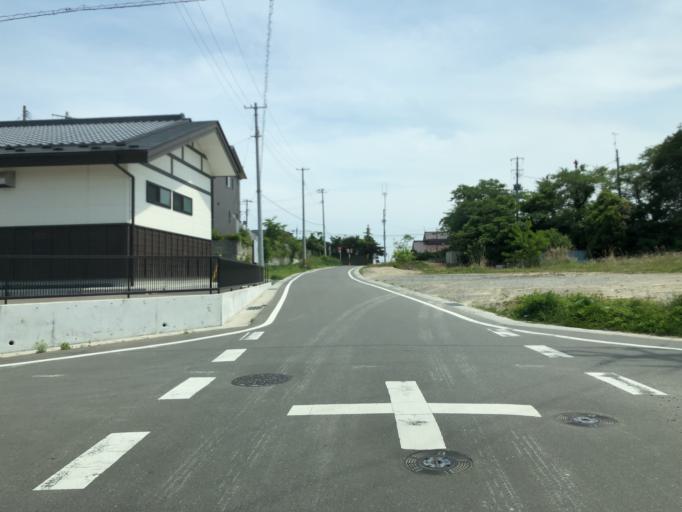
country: JP
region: Miyagi
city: Marumori
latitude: 37.8264
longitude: 140.9564
